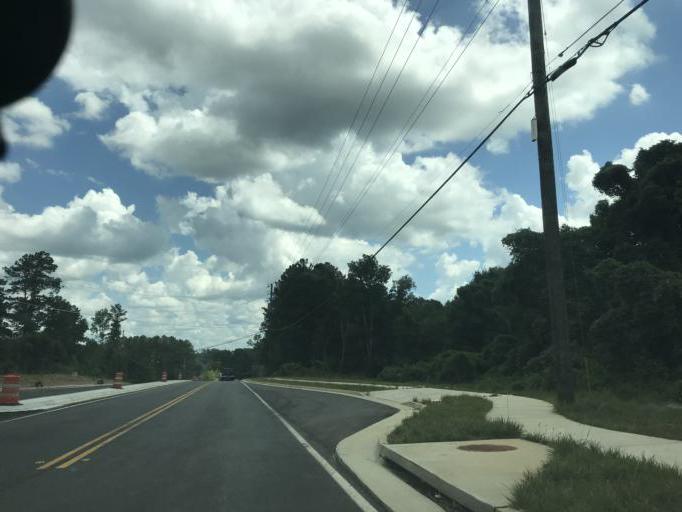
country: US
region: Georgia
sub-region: Forsyth County
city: Cumming
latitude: 34.2307
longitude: -84.1940
